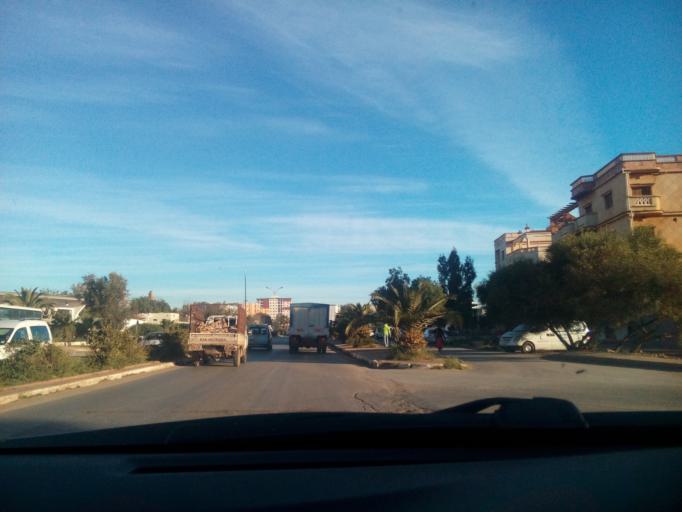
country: DZ
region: Oran
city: Oran
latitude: 35.6677
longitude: -0.6645
